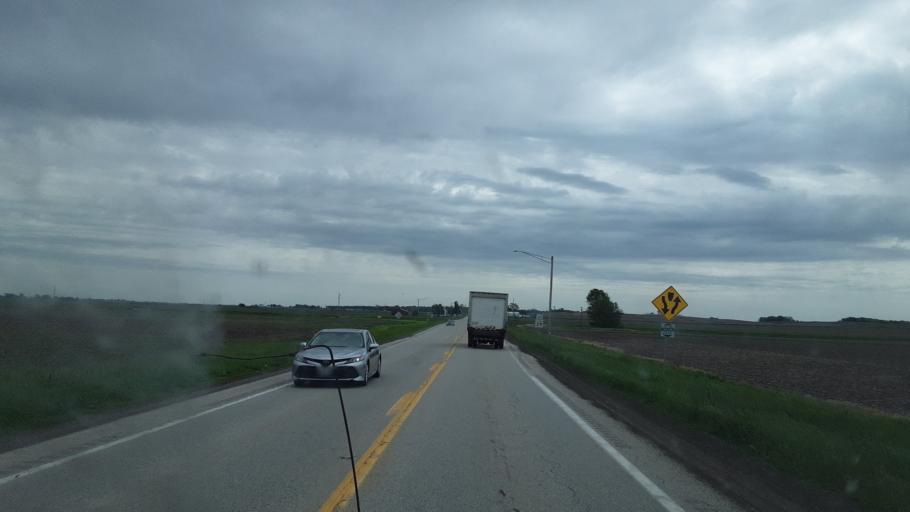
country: US
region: Illinois
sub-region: Mason County
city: Mason City
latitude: 40.3052
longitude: -89.6441
